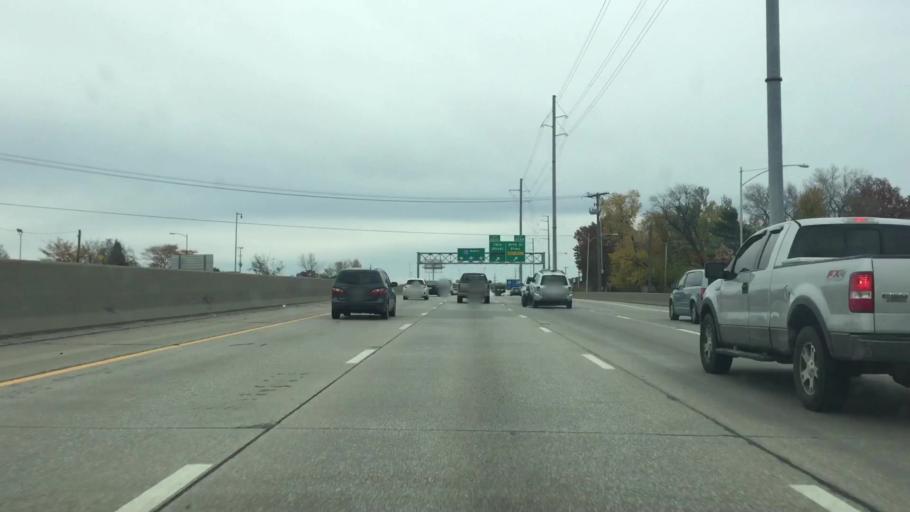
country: US
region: Kansas
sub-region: Johnson County
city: Lenexa
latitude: 38.9620
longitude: -94.7274
